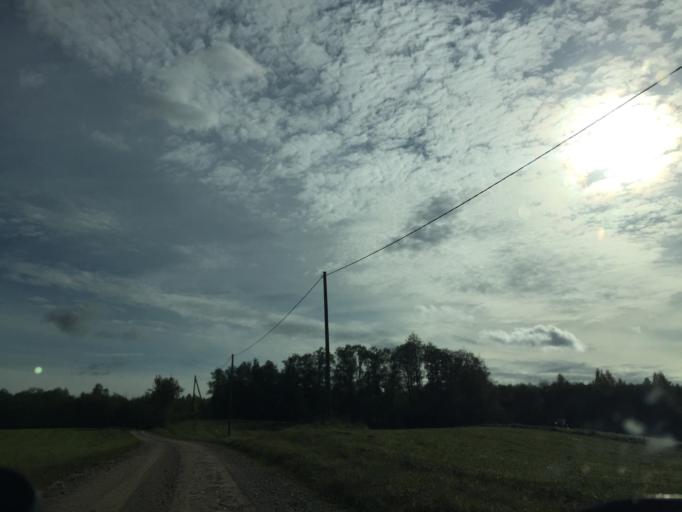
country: LV
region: Jaunpils
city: Jaunpils
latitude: 56.6061
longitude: 22.9978
